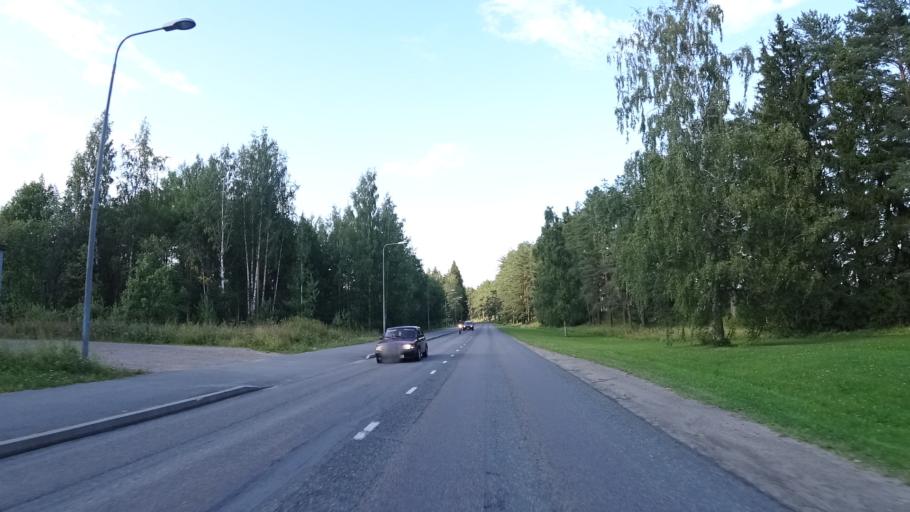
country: FI
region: South Karelia
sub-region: Imatra
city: Imatra
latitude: 61.1768
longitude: 28.7792
